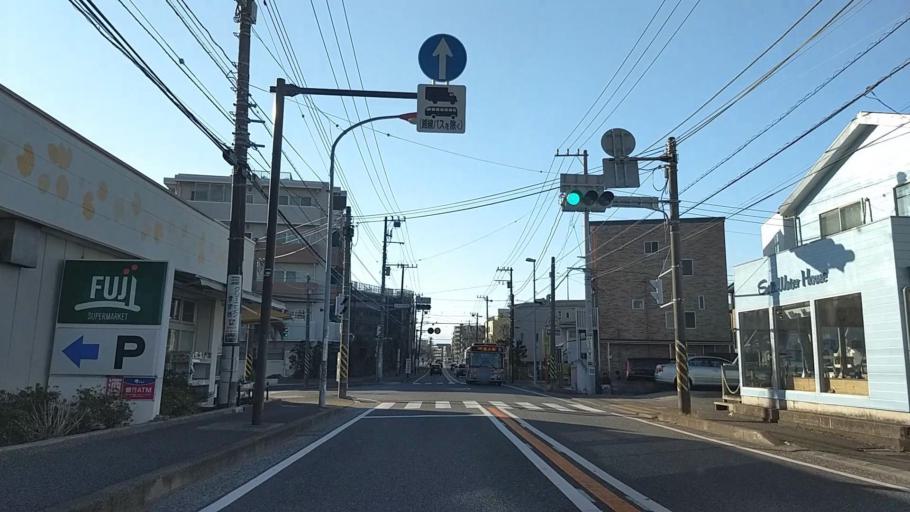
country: JP
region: Kanagawa
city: Fujisawa
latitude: 35.3247
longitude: 139.4868
